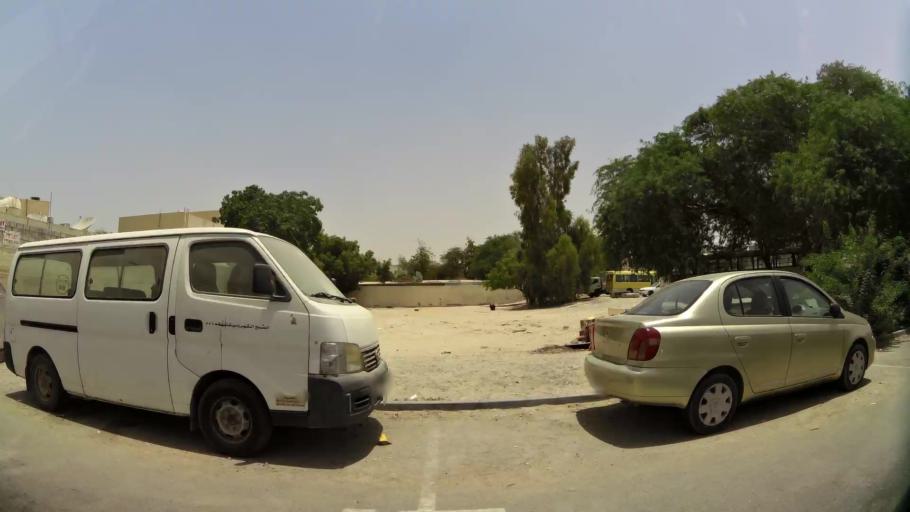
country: AE
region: Ash Shariqah
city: Sharjah
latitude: 25.2668
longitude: 55.4270
